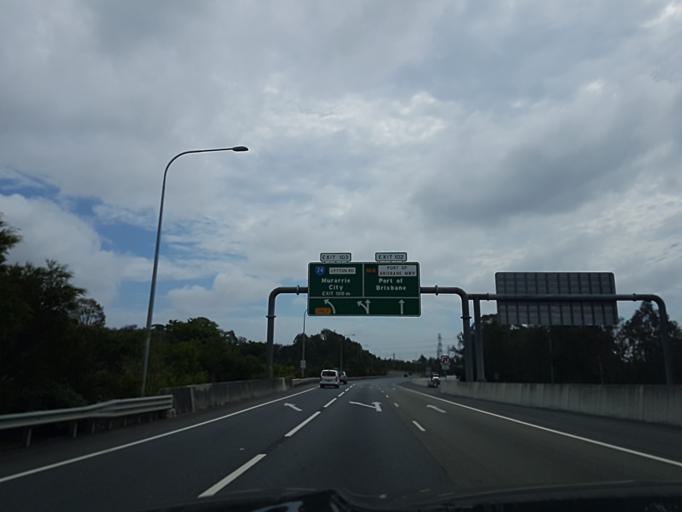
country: AU
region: Queensland
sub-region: Brisbane
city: Cannon Hill
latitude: -27.4546
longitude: 153.1114
